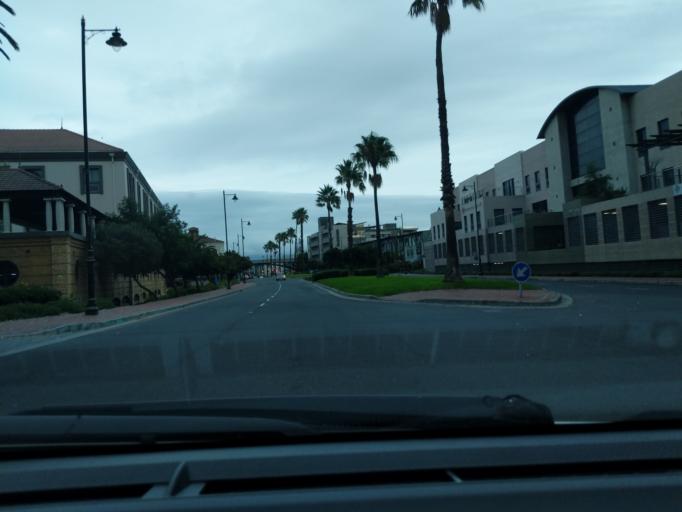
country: ZA
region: Western Cape
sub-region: City of Cape Town
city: Sunset Beach
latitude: -33.8902
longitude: 18.5182
